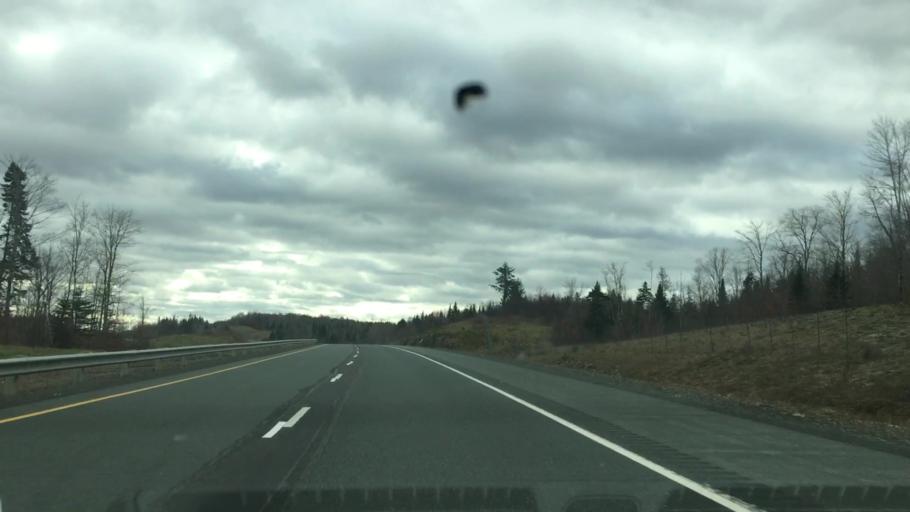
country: US
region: Maine
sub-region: Aroostook County
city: Fort Fairfield
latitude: 46.6434
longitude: -67.7443
